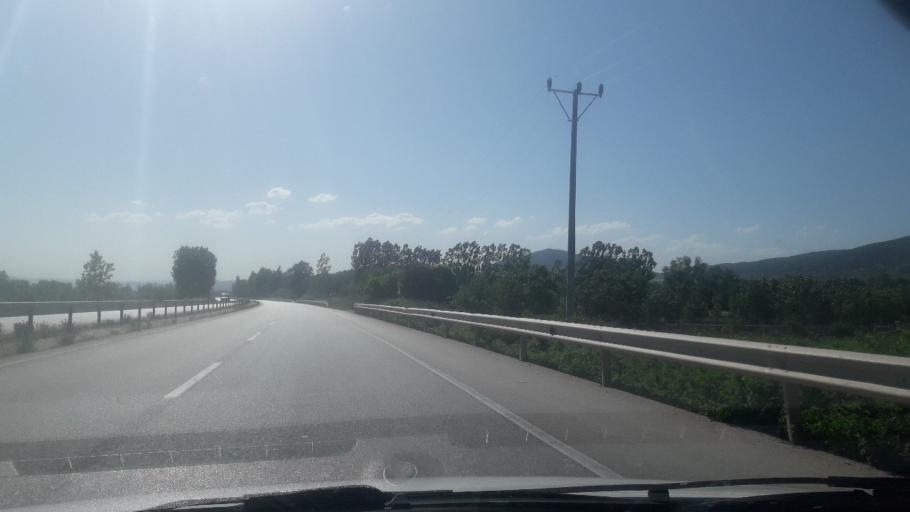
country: TR
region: Tokat
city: Dokmetepe
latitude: 40.3132
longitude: 36.2766
